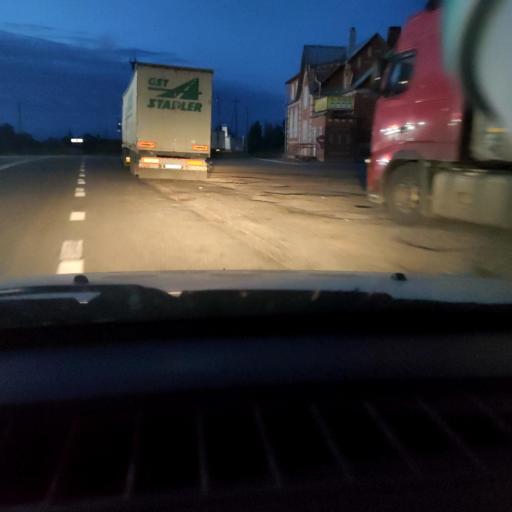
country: RU
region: Kirov
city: Kotel'nich
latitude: 58.3194
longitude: 48.3958
